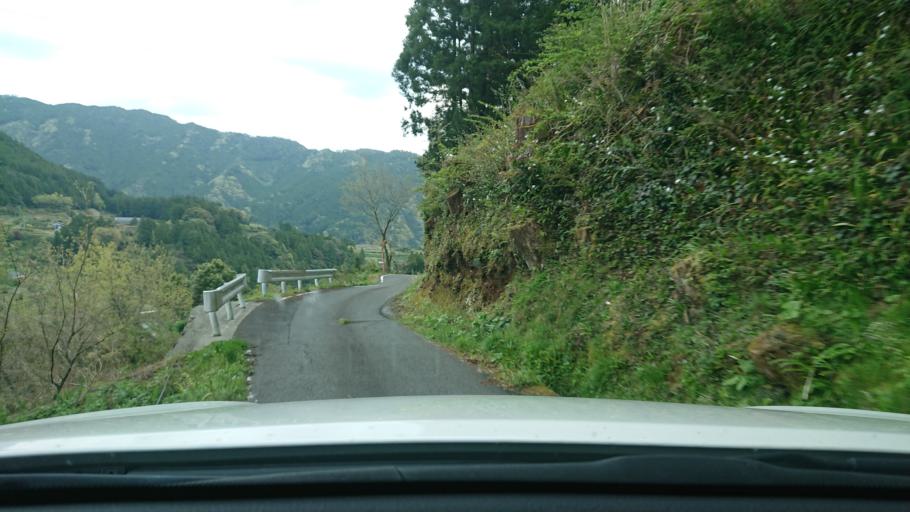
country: JP
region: Tokushima
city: Kamojimacho-jogejima
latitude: 33.8854
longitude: 134.3907
